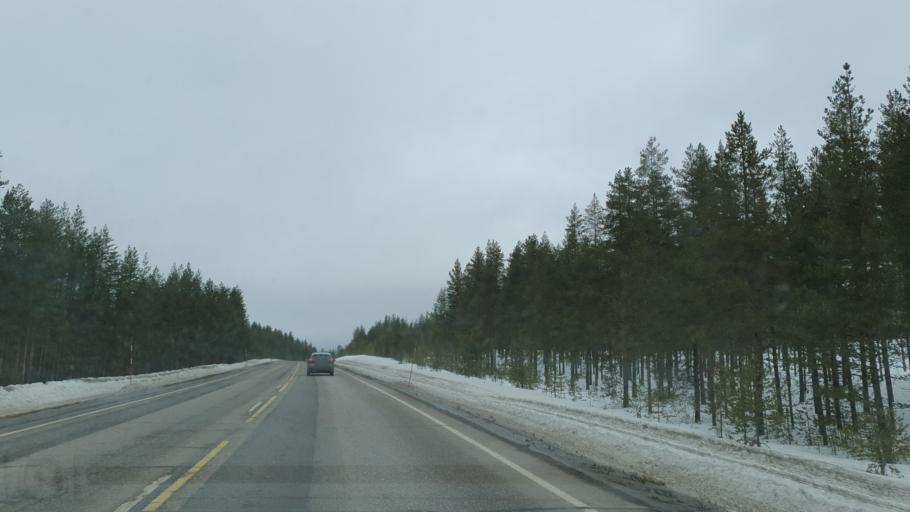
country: FI
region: Lapland
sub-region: Torniolaakso
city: Pello
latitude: 66.9197
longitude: 24.0913
